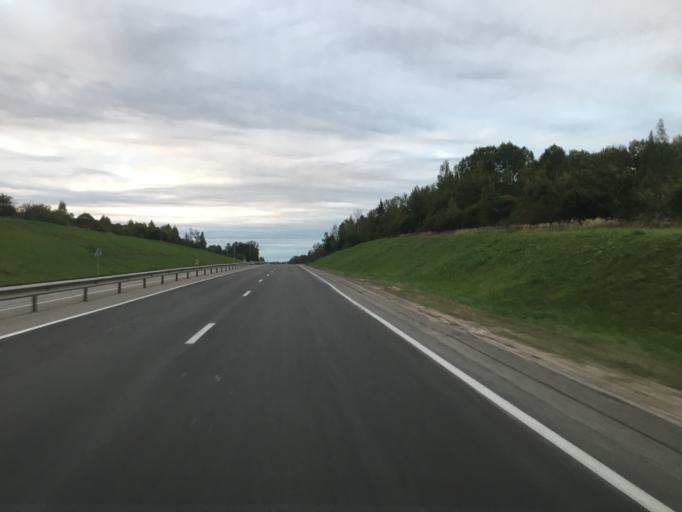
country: RU
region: Kaluga
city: Kaluga
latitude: 54.6027
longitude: 36.3174
